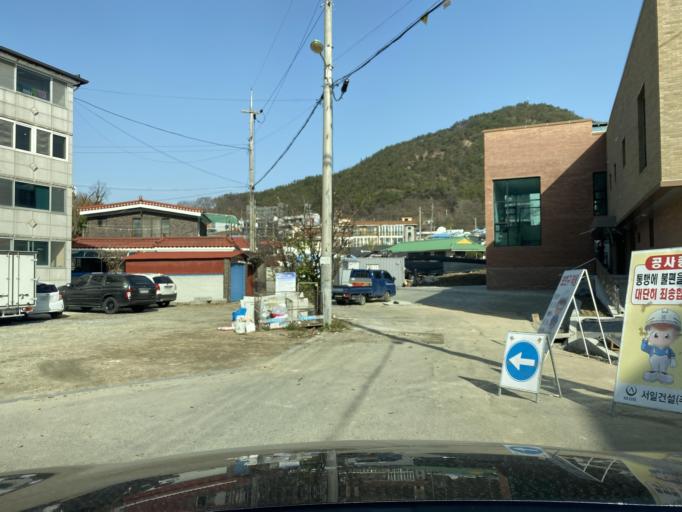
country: KR
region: Chungcheongnam-do
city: Yesan
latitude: 36.6829
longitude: 126.8463
